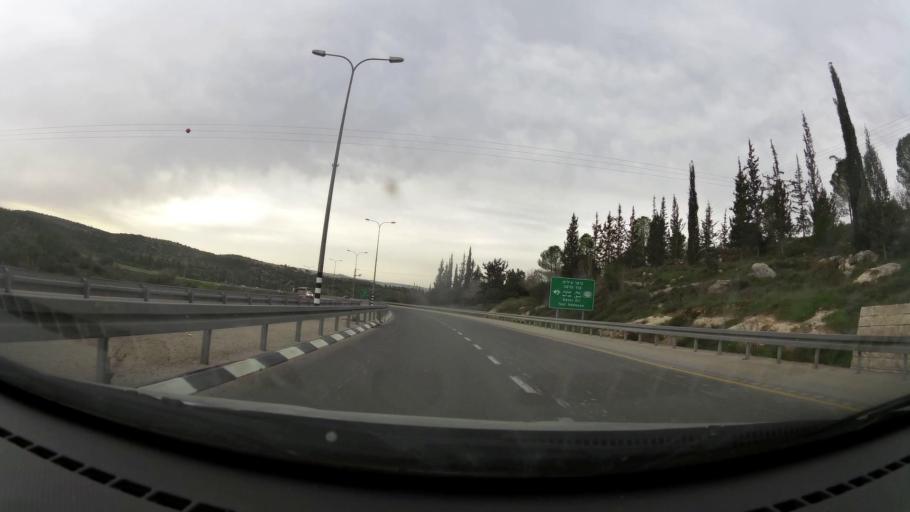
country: IL
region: Jerusalem
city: Bet Shemesh
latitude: 31.6937
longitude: 35.0097
